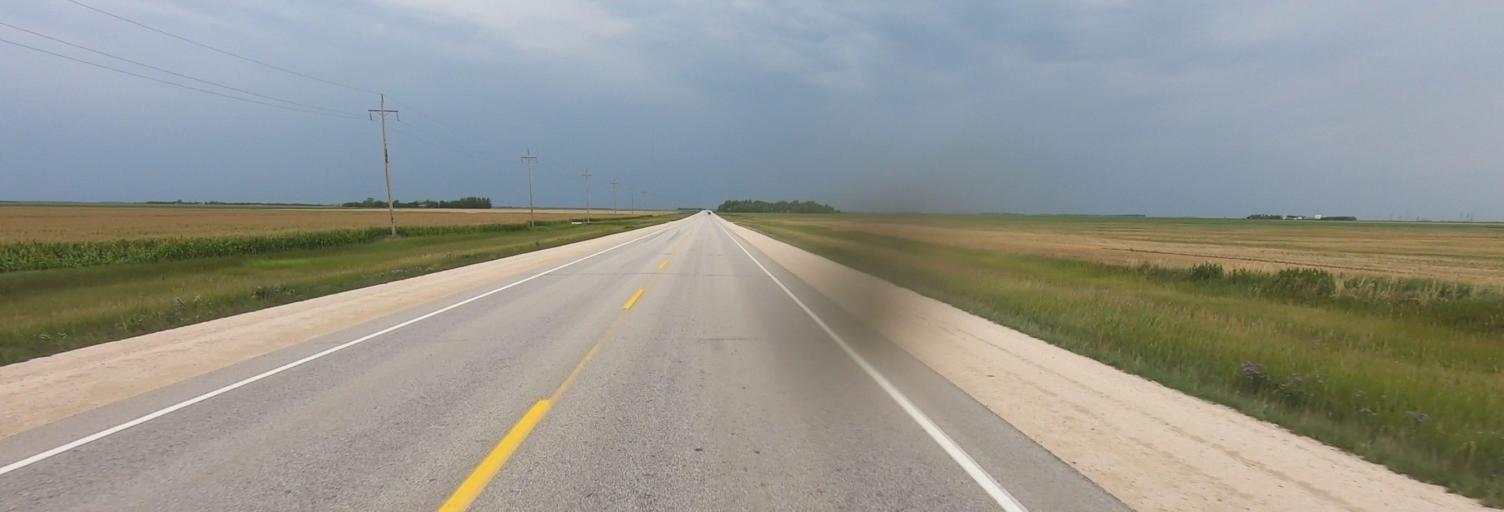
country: CA
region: Manitoba
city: Headingley
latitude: 49.7684
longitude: -97.3719
